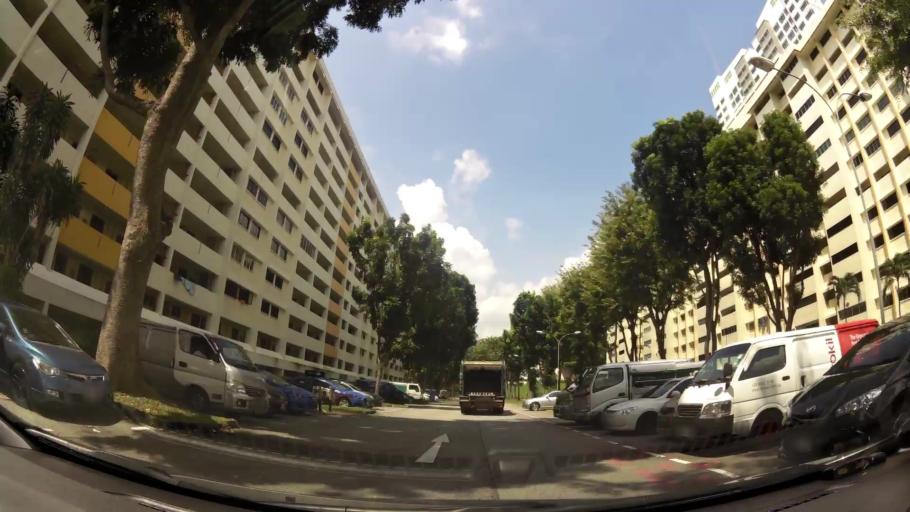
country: SG
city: Singapore
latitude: 1.3680
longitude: 103.8344
